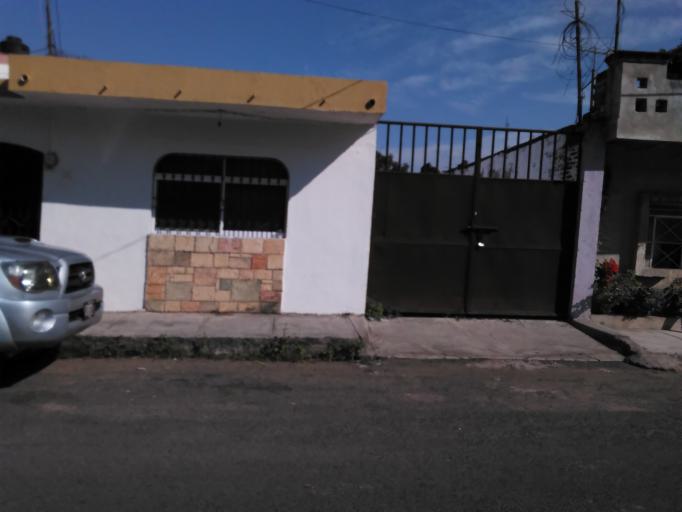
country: MX
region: Nayarit
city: Tepic
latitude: 21.4840
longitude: -104.8908
